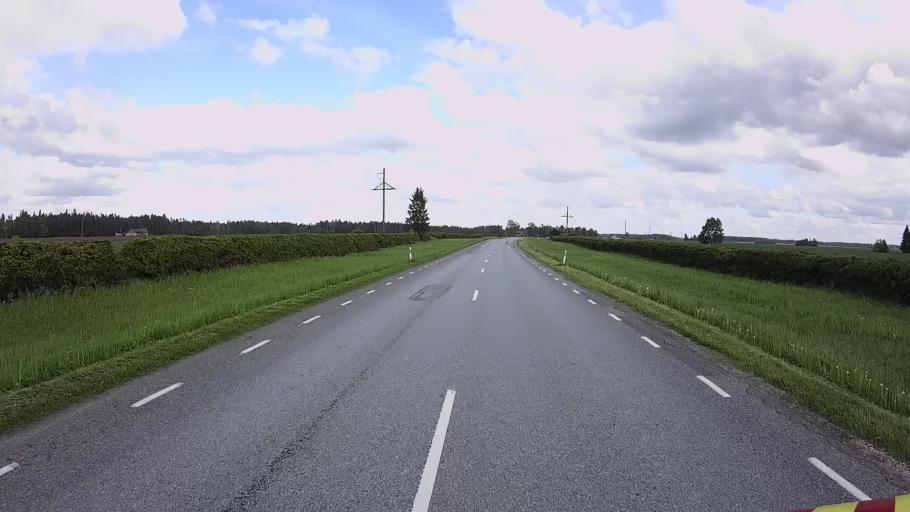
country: EE
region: Laeaene-Virumaa
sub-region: Vinni vald
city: Vinni
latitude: 59.2146
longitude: 26.5425
